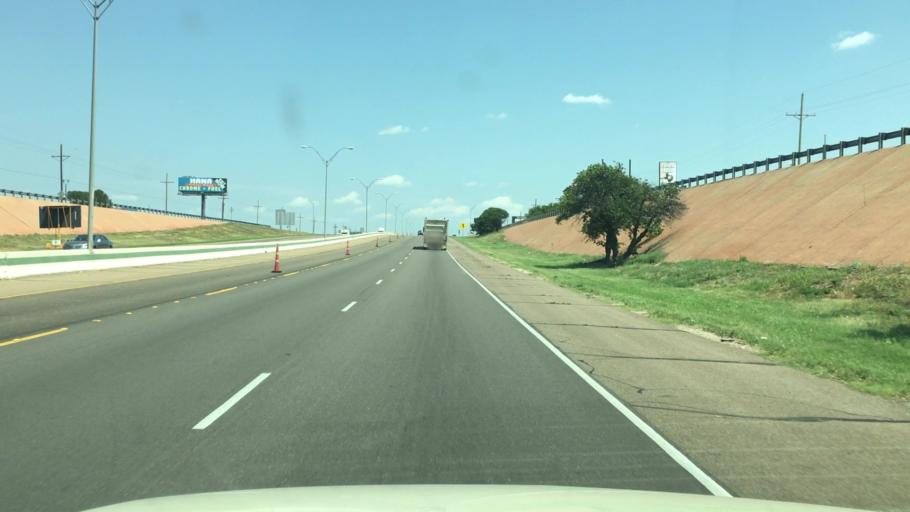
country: US
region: Texas
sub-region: Potter County
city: Amarillo
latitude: 35.1927
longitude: -101.7240
